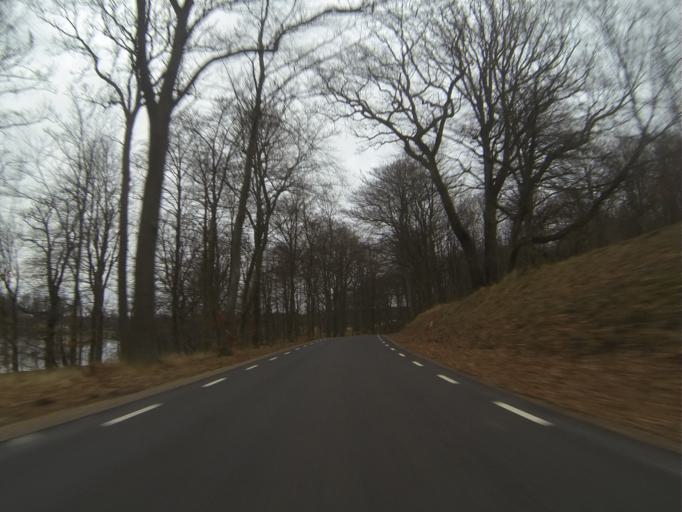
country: SE
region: Skane
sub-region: Lunds Kommun
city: Genarp
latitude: 55.5778
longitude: 13.4318
